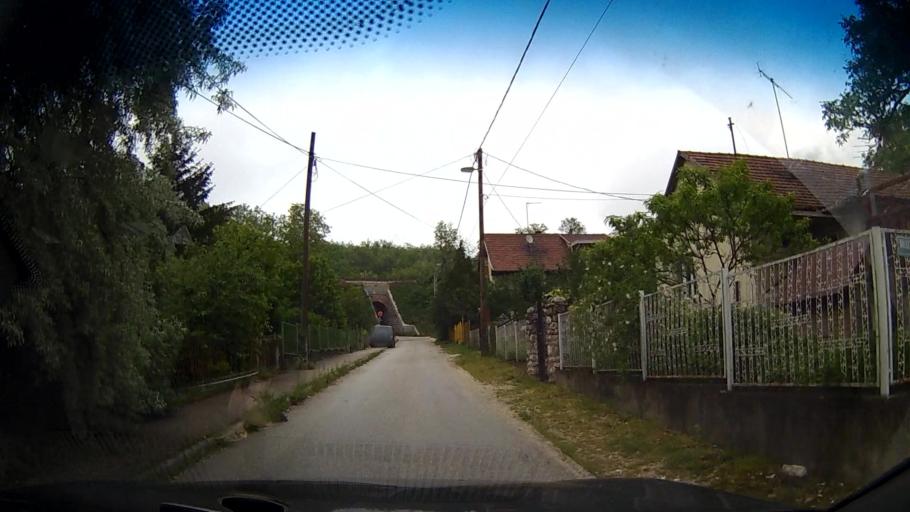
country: HU
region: Komarom-Esztergom
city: Piliscsev
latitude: 47.6567
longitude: 18.7894
